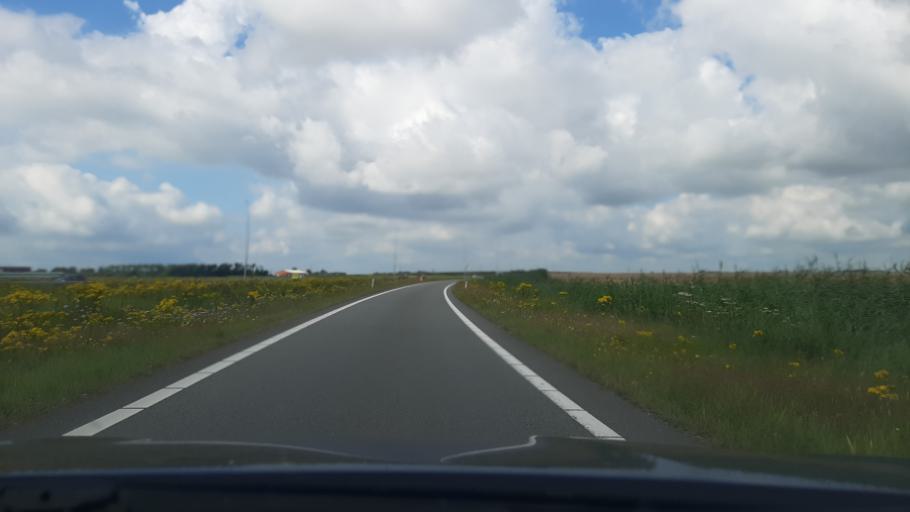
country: NL
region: Groningen
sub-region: Gemeente  Oldambt
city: Winschoten
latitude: 53.1875
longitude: 6.9723
